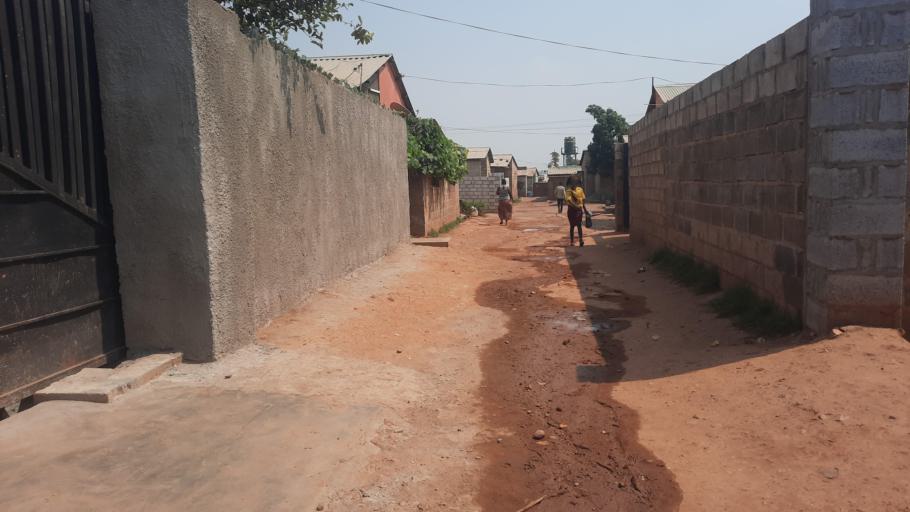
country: ZM
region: Lusaka
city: Lusaka
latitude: -15.4008
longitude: 28.3770
